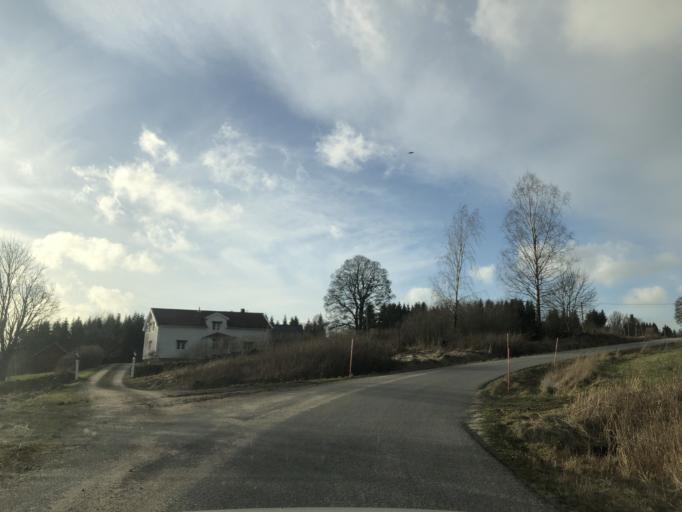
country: SE
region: Vaestra Goetaland
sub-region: Ulricehamns Kommun
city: Ulricehamn
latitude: 57.8045
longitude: 13.3661
